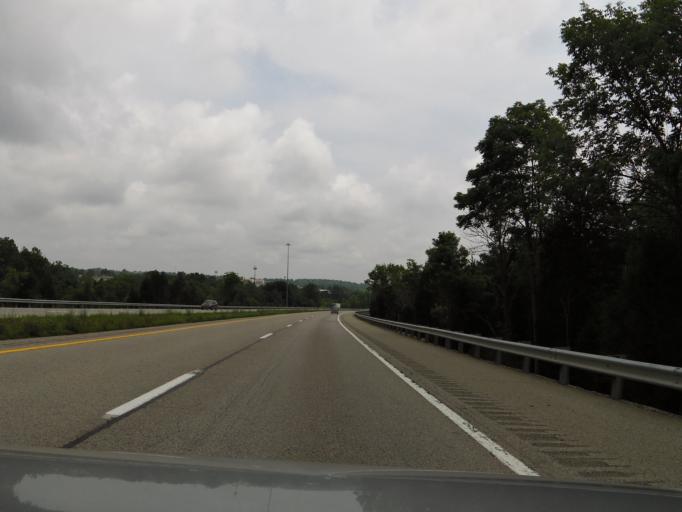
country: US
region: Kentucky
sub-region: Grayson County
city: Leitchfield
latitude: 37.4638
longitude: -86.3014
